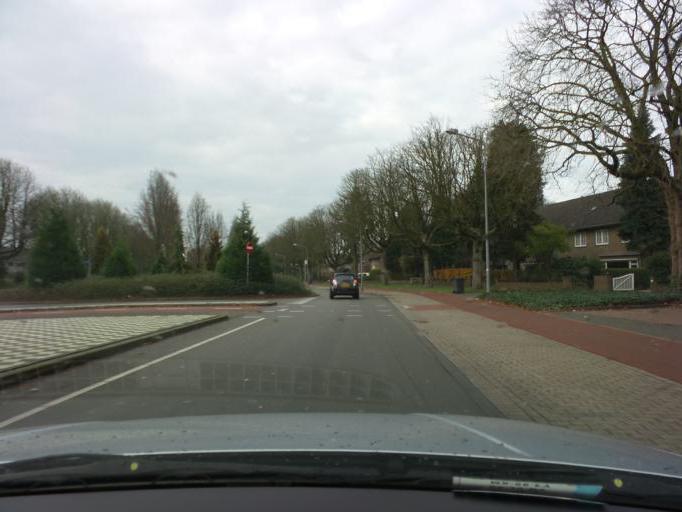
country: NL
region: North Holland
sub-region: Gemeente Hilversum
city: Hilversum
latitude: 52.2352
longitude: 5.1821
